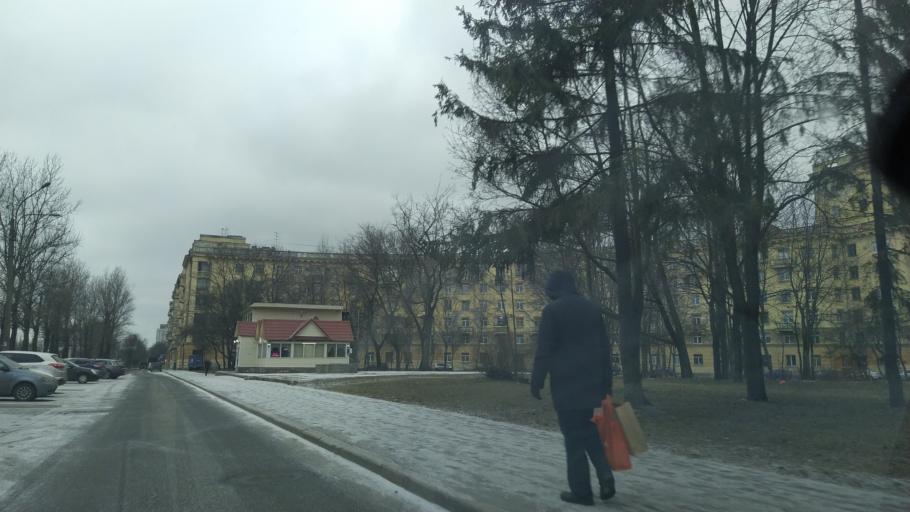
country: RU
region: St.-Petersburg
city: Kupchino
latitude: 59.8353
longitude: 30.3369
